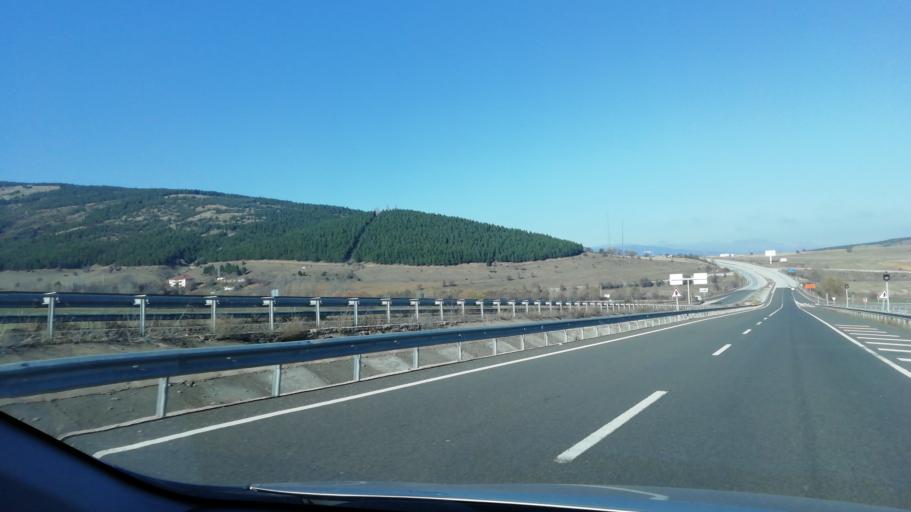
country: TR
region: Karabuk
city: Gozyeri
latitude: 40.8728
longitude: 32.5793
